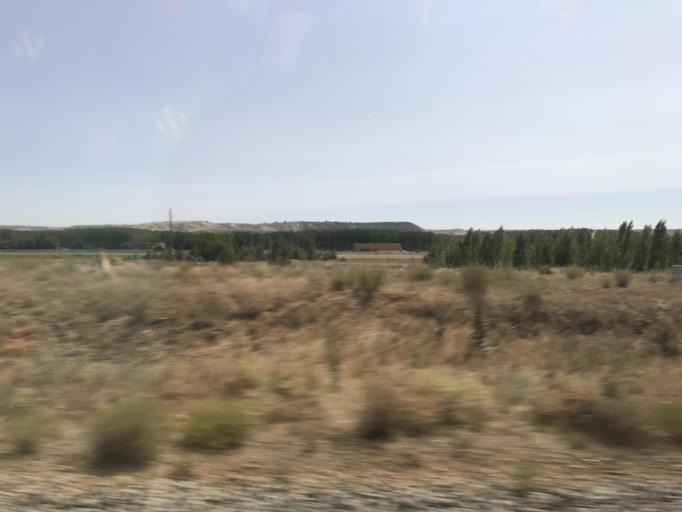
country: ES
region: Castille and Leon
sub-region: Provincia de Palencia
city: Villodrigo
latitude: 42.1581
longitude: -4.0866
